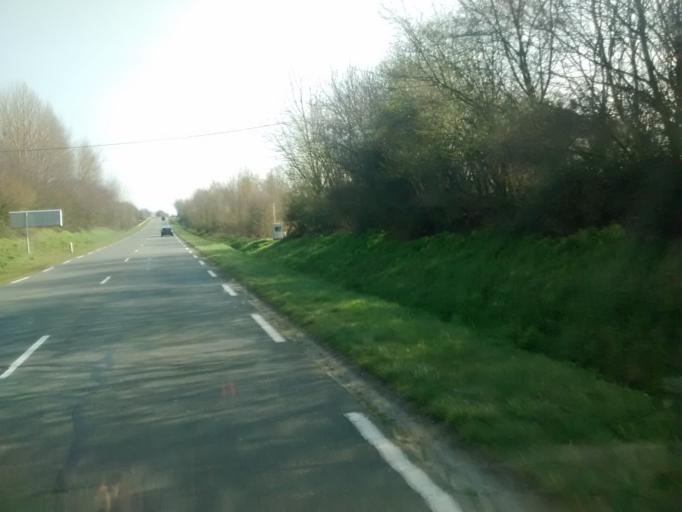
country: FR
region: Brittany
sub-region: Departement d'Ille-et-Vilaine
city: Chavagne
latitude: 48.0718
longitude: -1.7879
